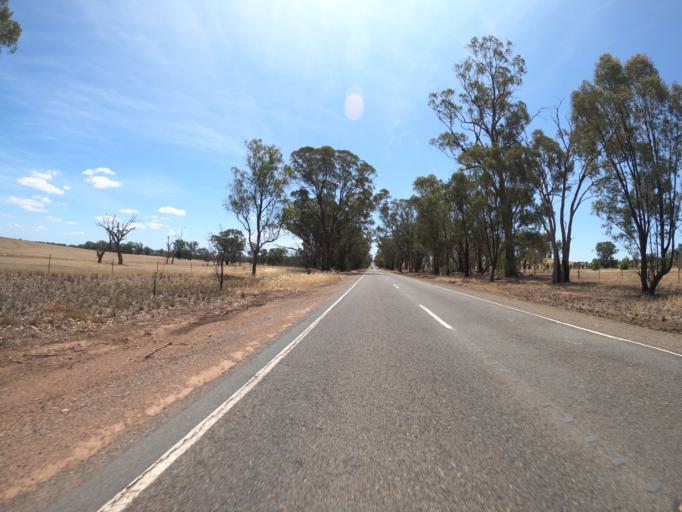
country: AU
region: Victoria
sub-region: Benalla
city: Benalla
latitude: -36.3588
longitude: 145.9666
